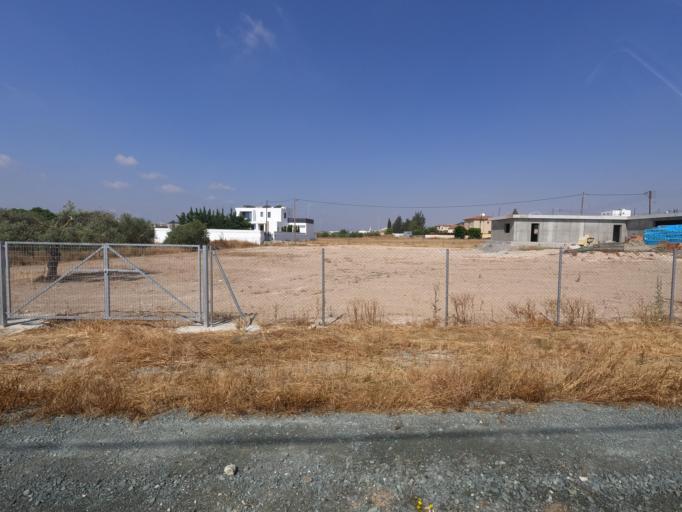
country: CY
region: Lefkosia
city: Lympia
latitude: 34.9985
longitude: 33.4743
